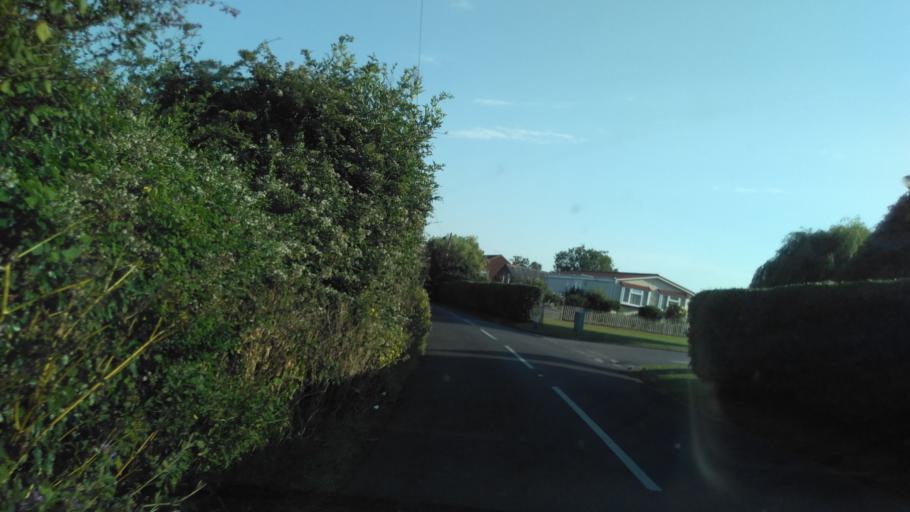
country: GB
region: England
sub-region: Kent
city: Whitstable
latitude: 51.3408
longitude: 1.0009
